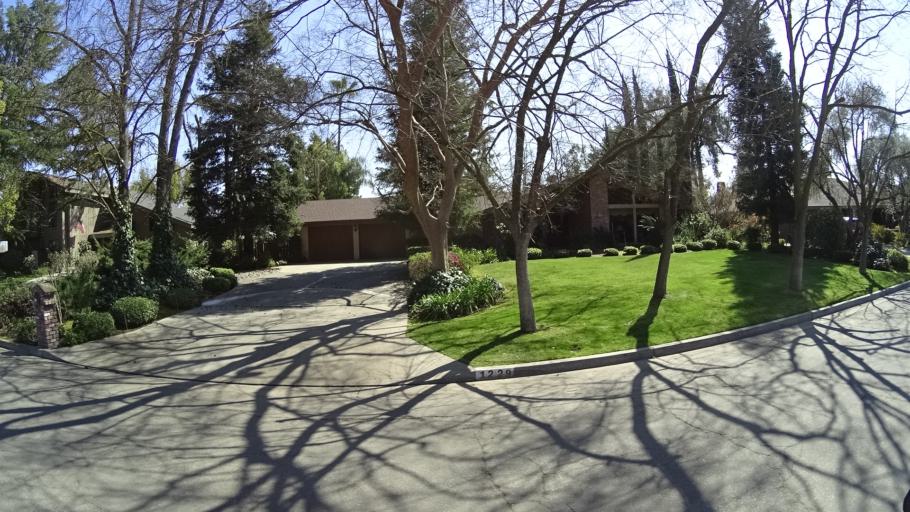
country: US
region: California
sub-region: Fresno County
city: Fresno
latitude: 36.8474
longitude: -119.8139
